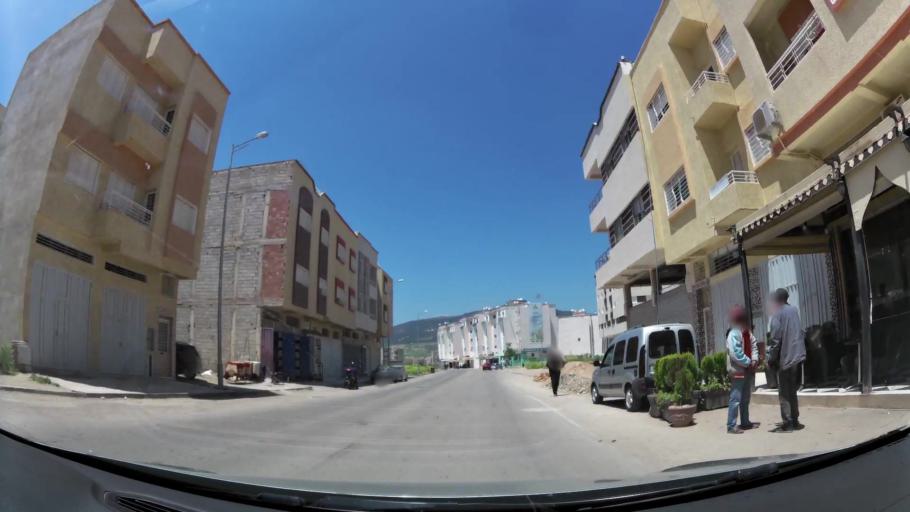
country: MA
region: Fes-Boulemane
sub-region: Fes
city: Fes
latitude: 34.0357
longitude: -5.0439
